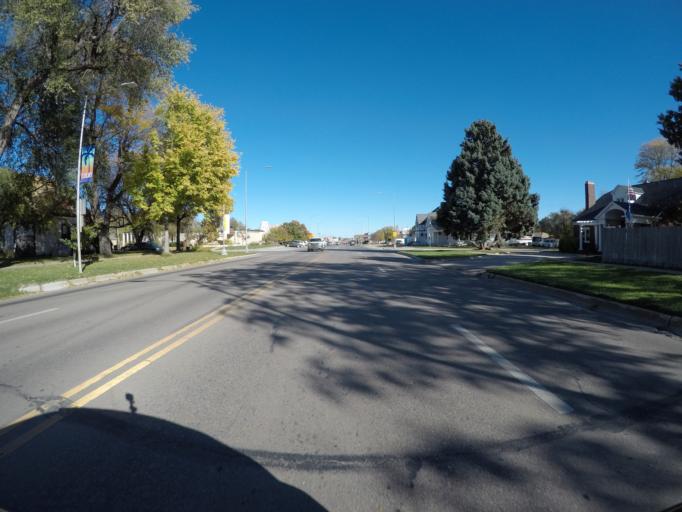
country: US
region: Kansas
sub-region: Thomas County
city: Colby
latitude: 39.3970
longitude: -101.0501
